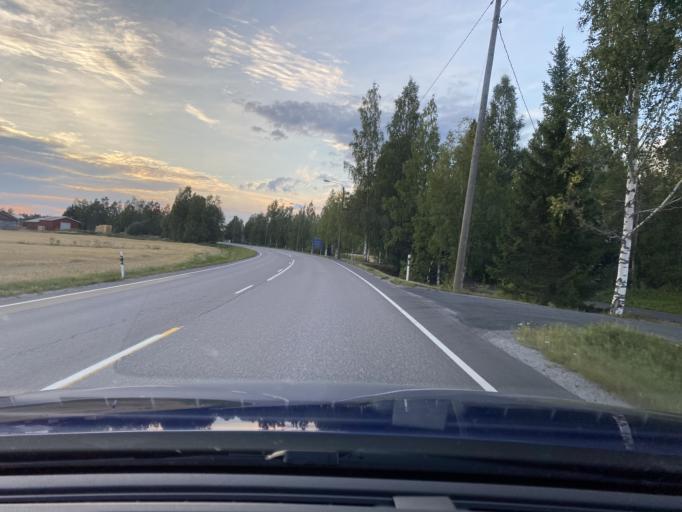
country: FI
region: Satakunta
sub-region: Pohjois-Satakunta
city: Kankaanpaeae
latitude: 61.7591
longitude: 22.5037
